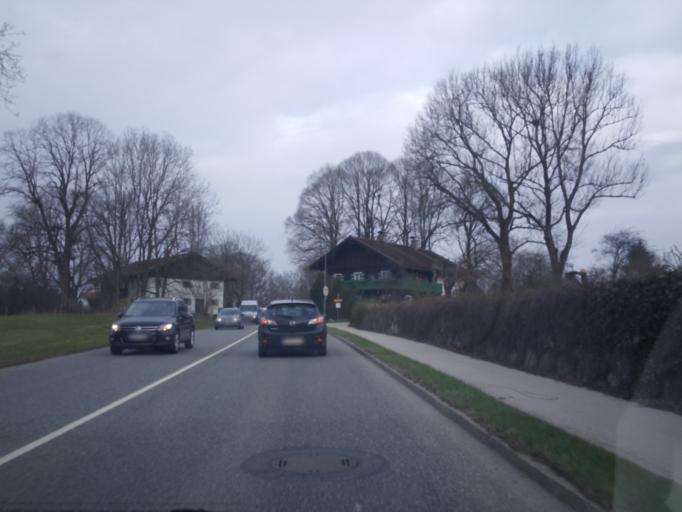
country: DE
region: Bavaria
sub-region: Upper Bavaria
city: Penzberg
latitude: 47.7675
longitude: 11.3511
